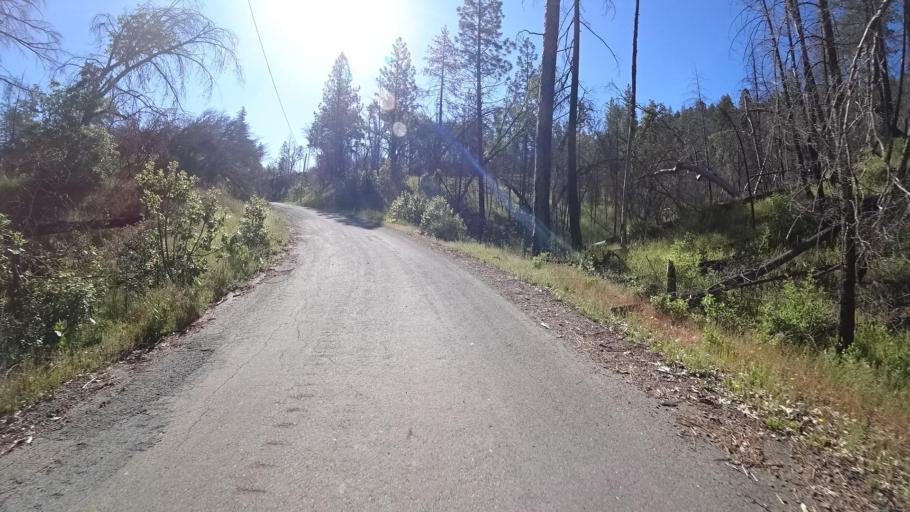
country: US
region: California
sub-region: Lake County
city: Upper Lake
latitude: 39.4030
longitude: -122.9672
